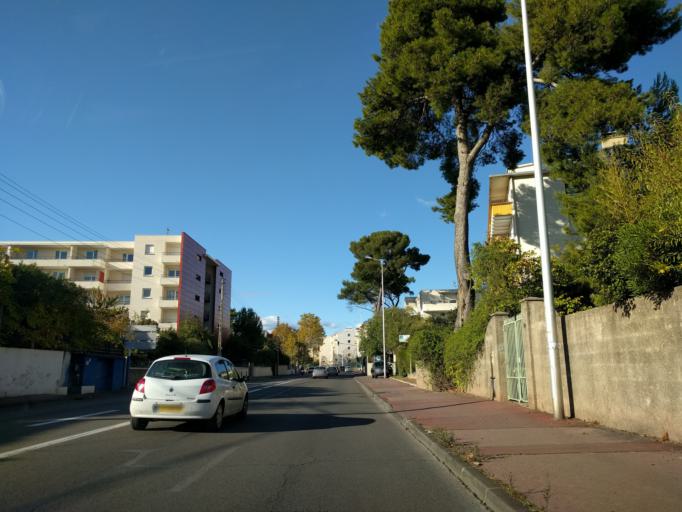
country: FR
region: Languedoc-Roussillon
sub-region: Departement de l'Herault
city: Montpellier
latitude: 43.6245
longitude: 3.8618
